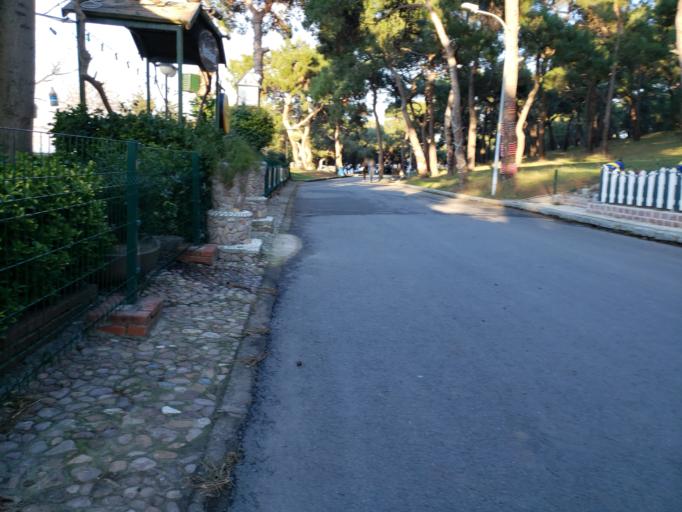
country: TR
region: Istanbul
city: Adalan
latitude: 40.8833
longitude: 29.0918
